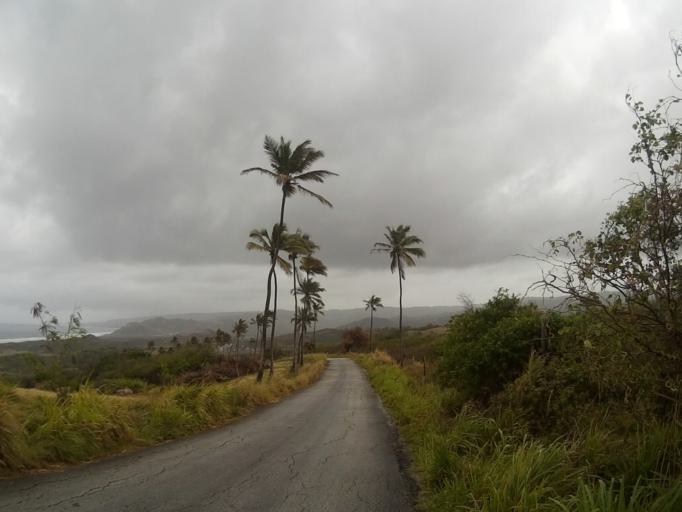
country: BB
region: Saint Andrew
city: Greenland
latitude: 13.2713
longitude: -59.5771
